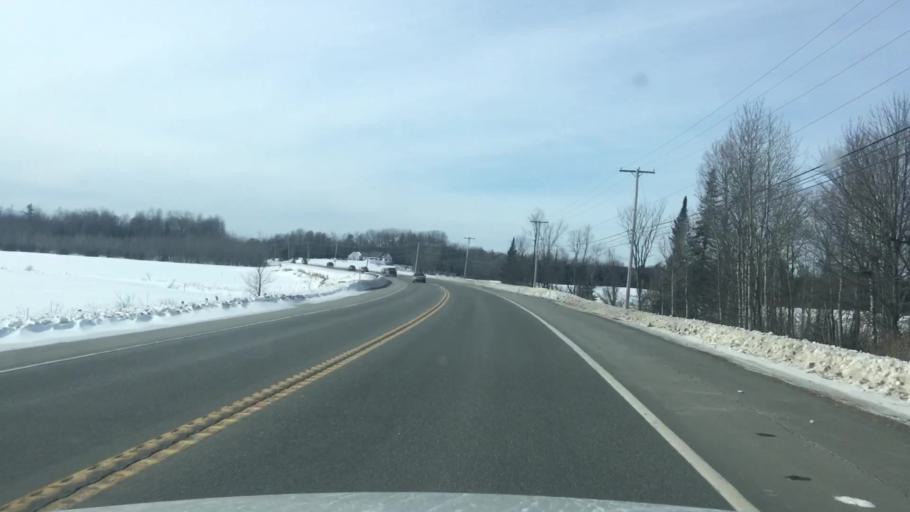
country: US
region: Maine
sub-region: Penobscot County
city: Kenduskeag
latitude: 44.9100
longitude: -68.8975
